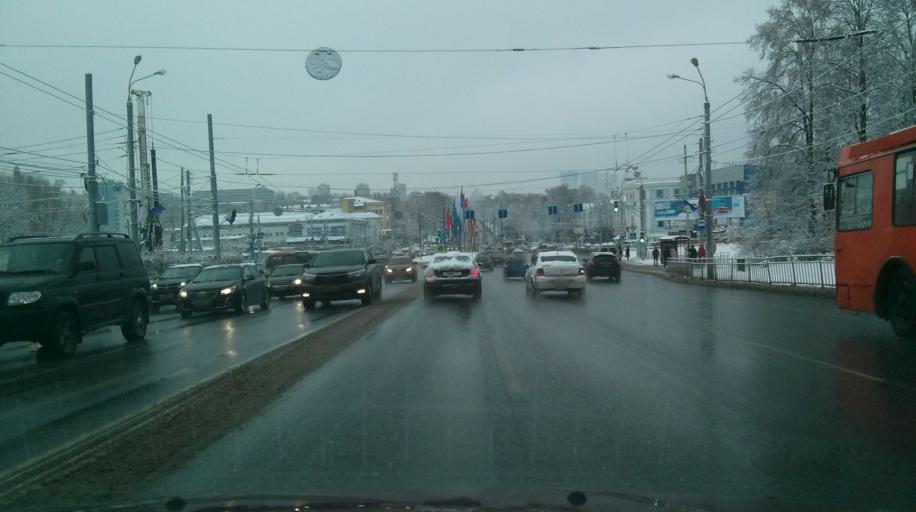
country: RU
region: Nizjnij Novgorod
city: Nizhniy Novgorod
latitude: 56.2568
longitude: 43.9710
